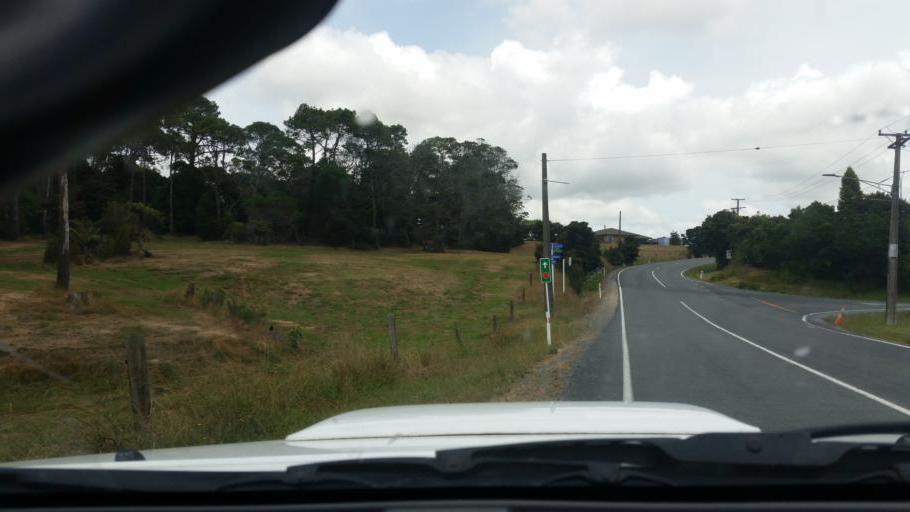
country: NZ
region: Auckland
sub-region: Auckland
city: Wellsford
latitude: -36.1290
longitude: 174.5661
